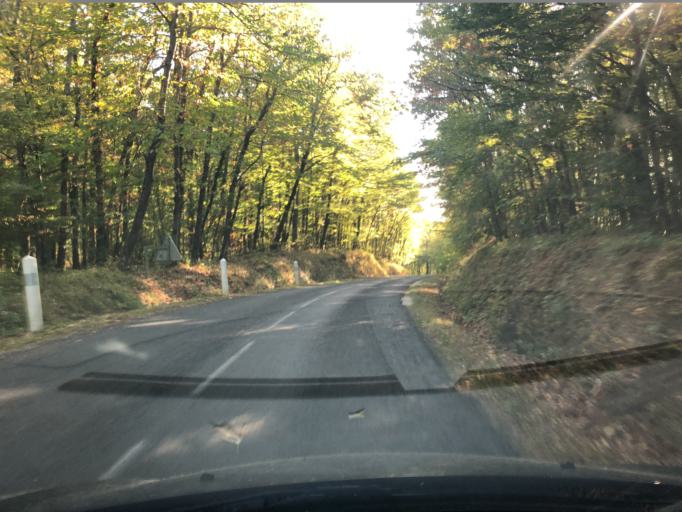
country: FR
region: Centre
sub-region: Departement d'Indre-et-Loire
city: Neuvy-le-Roi
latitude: 47.5878
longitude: 0.5967
